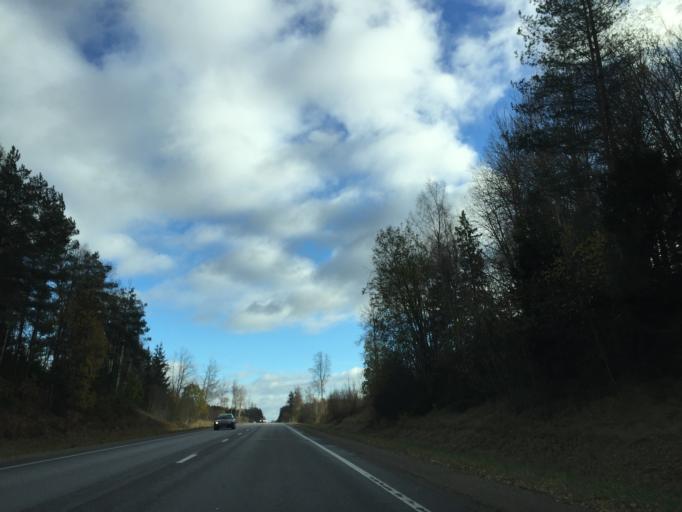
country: LV
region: Tukuma Rajons
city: Tukums
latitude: 56.9918
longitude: 23.0216
